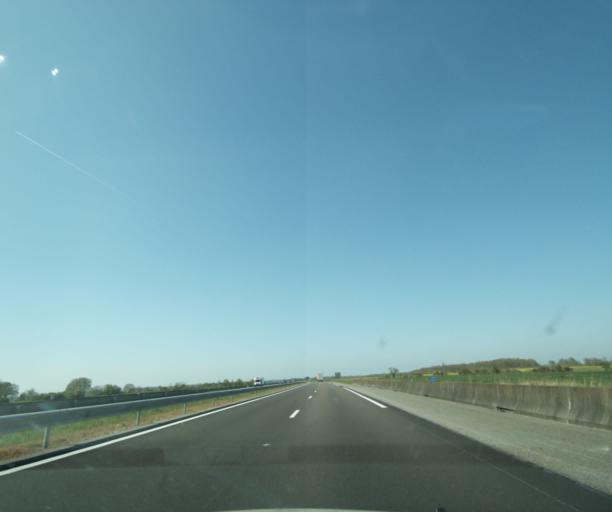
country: FR
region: Centre
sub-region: Departement du Loiret
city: Briare
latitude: 47.6270
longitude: 2.7904
